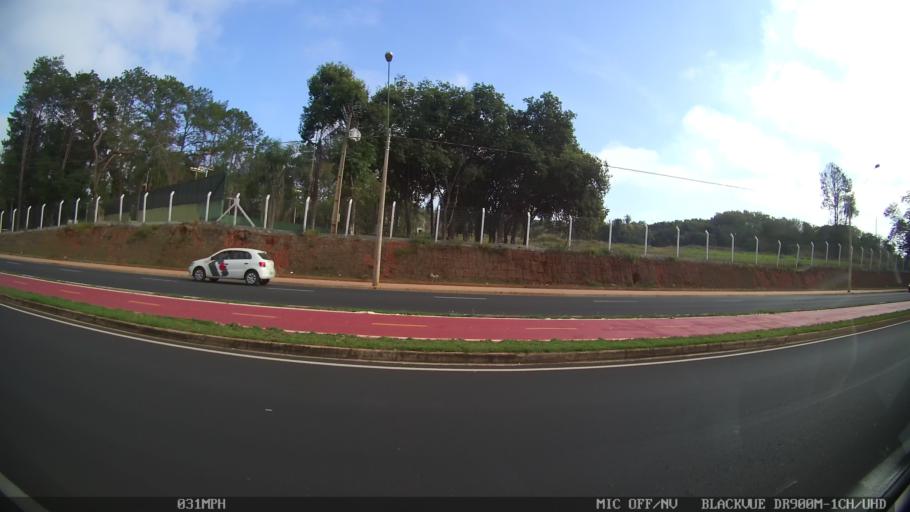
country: BR
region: Sao Paulo
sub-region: Sao Jose Do Rio Preto
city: Sao Jose do Rio Preto
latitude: -20.8101
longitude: -49.4316
